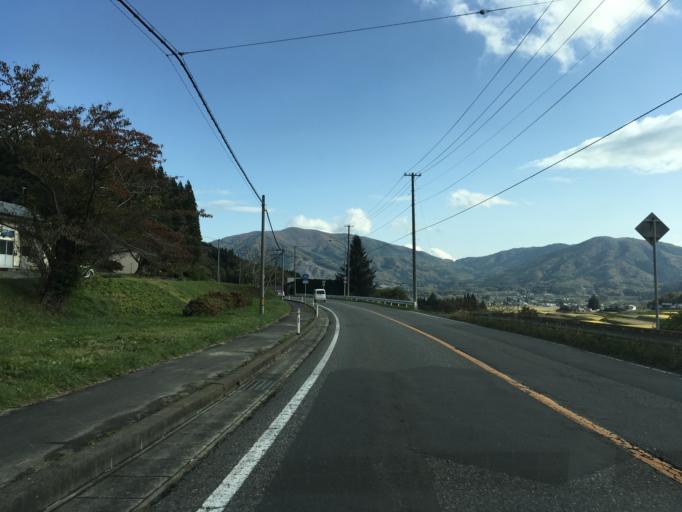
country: JP
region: Iwate
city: Tono
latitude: 39.3358
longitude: 141.4455
